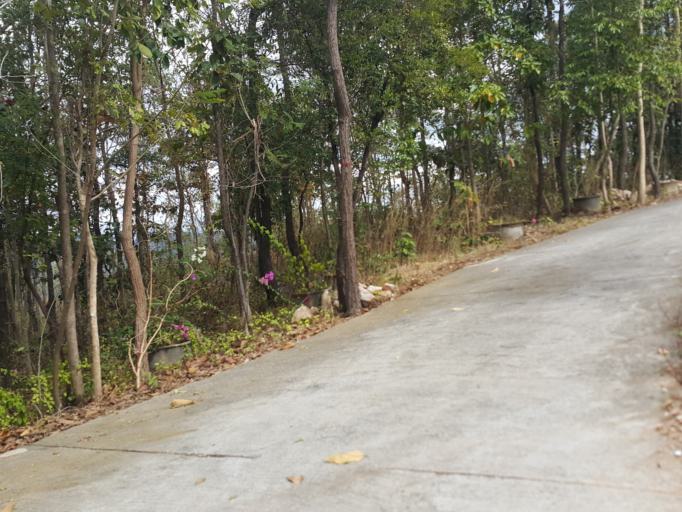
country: TH
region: Chiang Mai
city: San Sai
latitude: 18.8699
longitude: 99.1432
